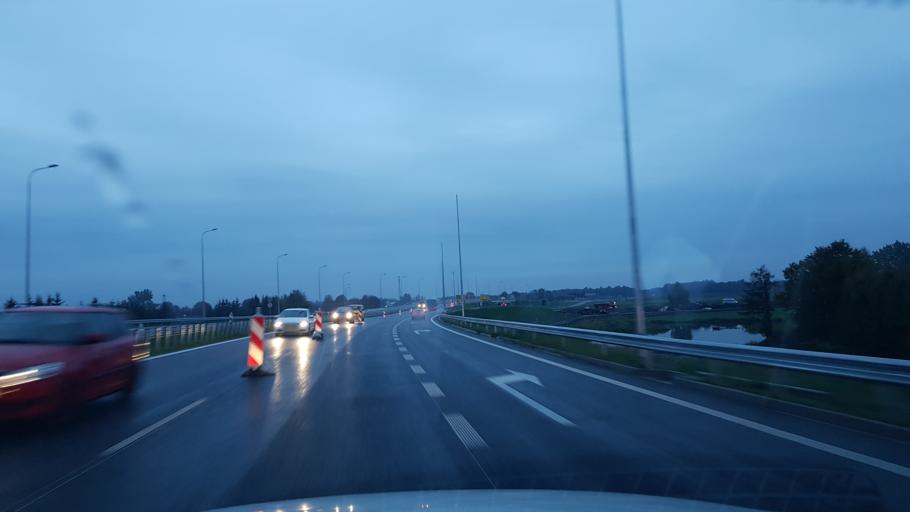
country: PL
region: West Pomeranian Voivodeship
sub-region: Powiat gryficki
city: Ploty
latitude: 53.8158
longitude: 15.2504
